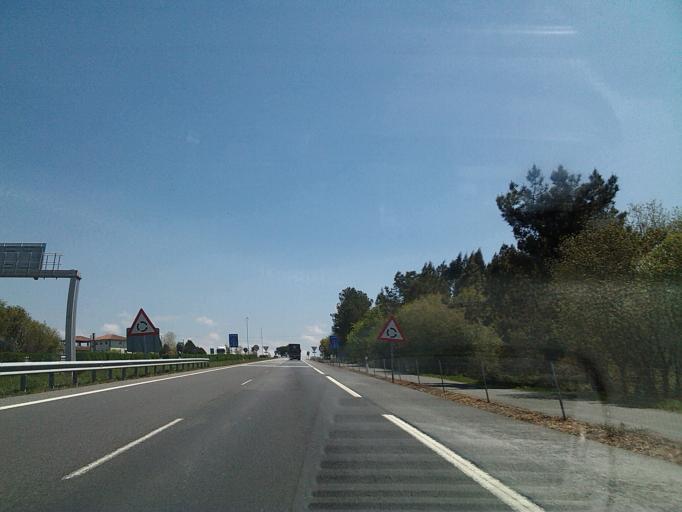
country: ES
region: Galicia
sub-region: Provincia da Coruna
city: Oroso
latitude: 42.9139
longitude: -8.4184
